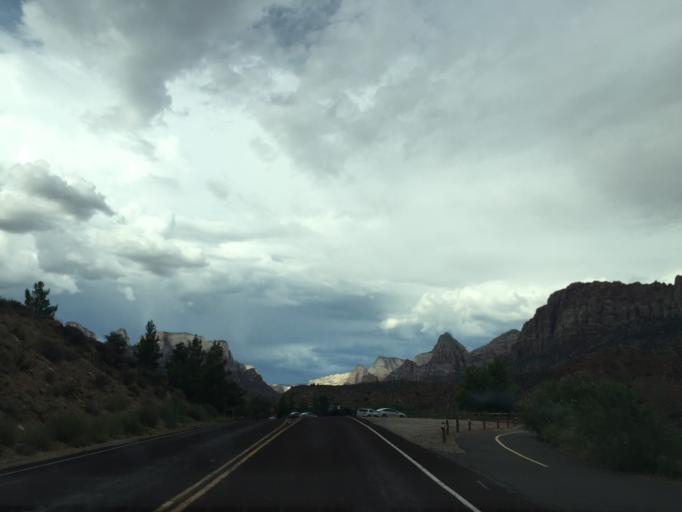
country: US
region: Utah
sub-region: Washington County
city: Hildale
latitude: 37.1657
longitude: -113.0142
